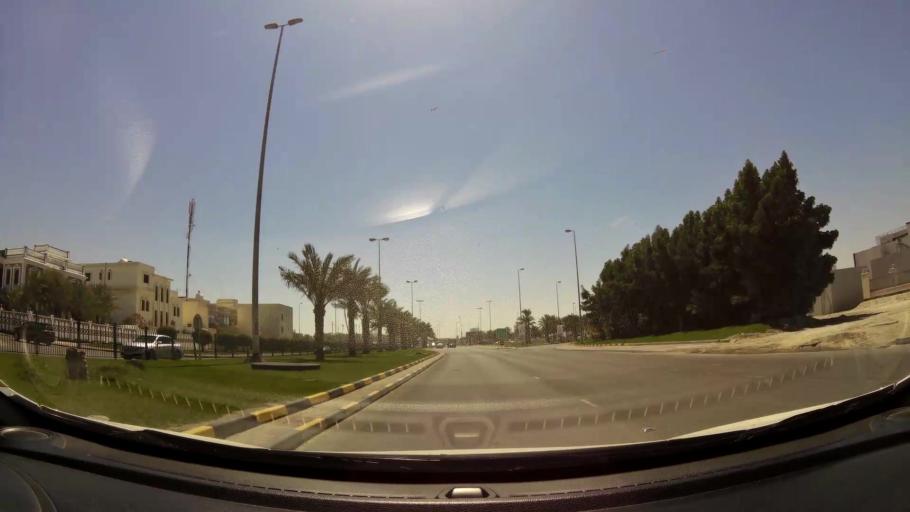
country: BH
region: Muharraq
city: Al Muharraq
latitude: 26.2622
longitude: 50.6031
